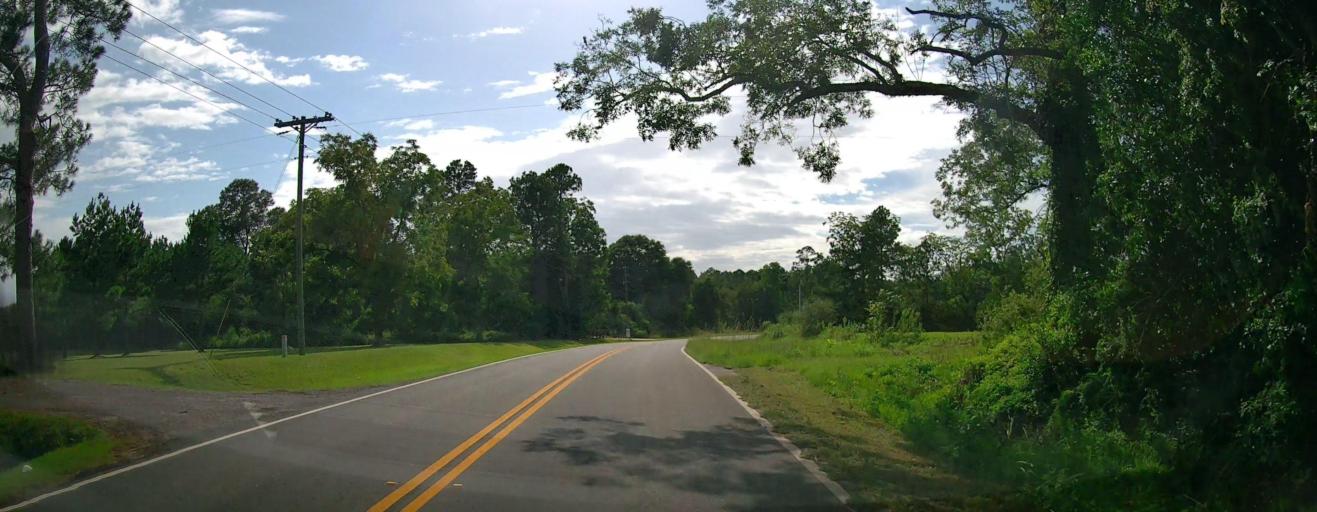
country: US
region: Georgia
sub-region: Coffee County
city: Douglas
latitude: 31.4484
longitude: -82.8756
